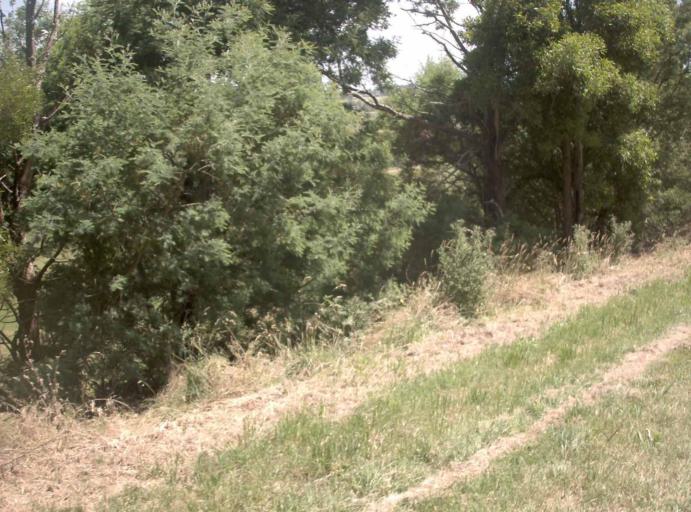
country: AU
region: Victoria
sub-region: Baw Baw
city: Warragul
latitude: -38.2525
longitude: 145.9103
